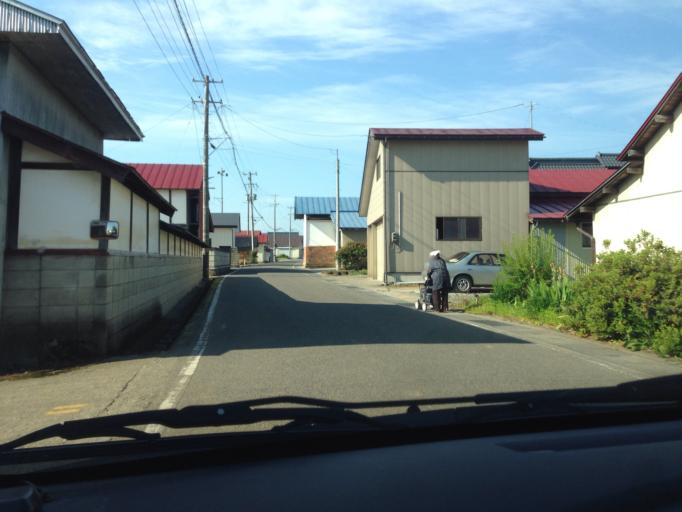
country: JP
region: Fukushima
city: Kitakata
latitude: 37.5514
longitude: 139.8177
